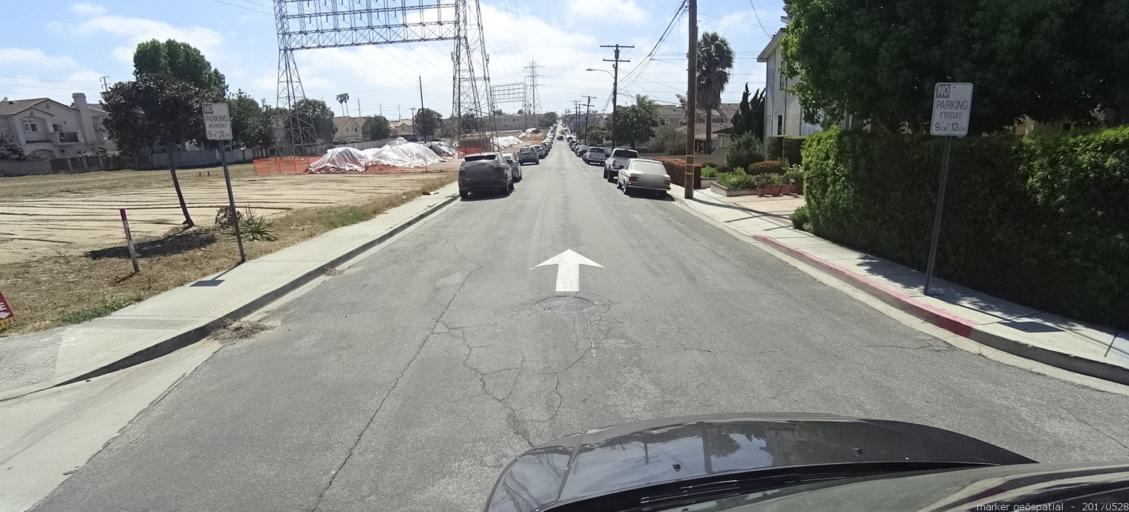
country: US
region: California
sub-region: Los Angeles County
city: Lawndale
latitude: 33.8700
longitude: -118.3623
